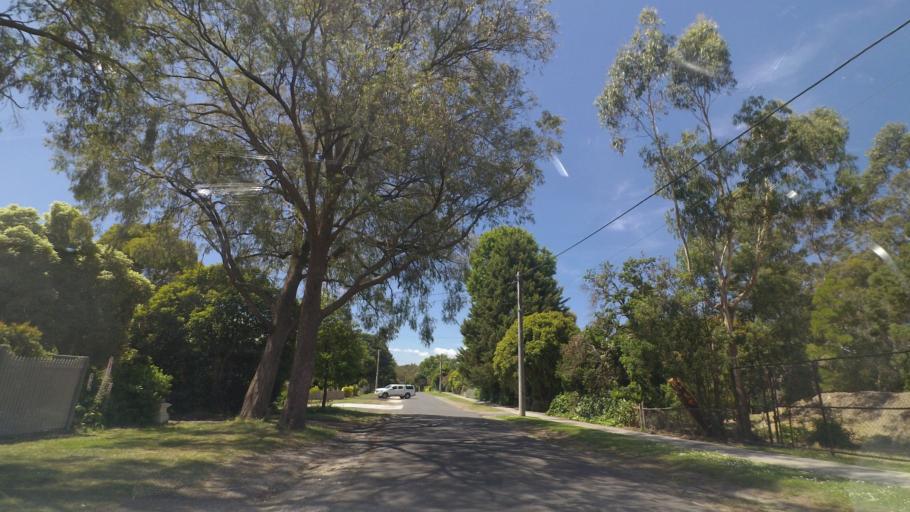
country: AU
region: Victoria
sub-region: Yarra Ranges
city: Montrose
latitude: -37.8068
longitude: 145.3436
